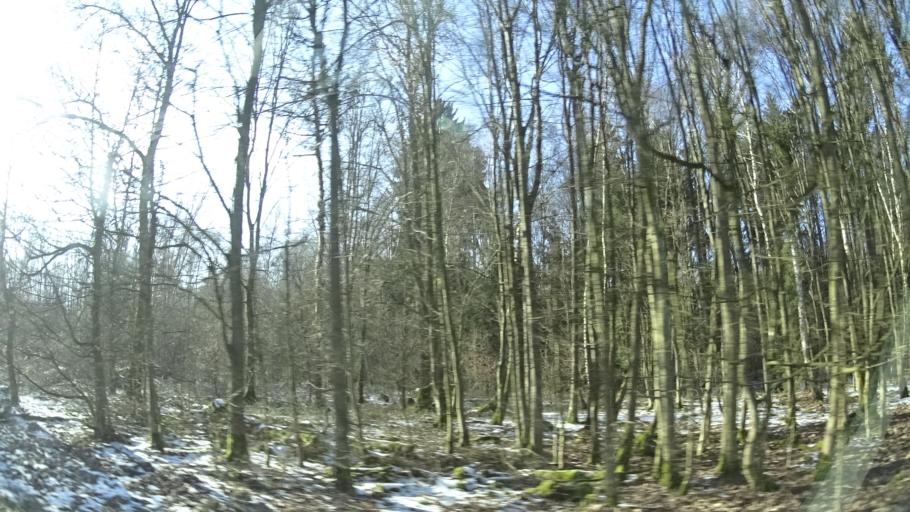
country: DE
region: Bavaria
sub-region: Regierungsbezirk Unterfranken
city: Motten
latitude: 50.4188
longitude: 9.7337
